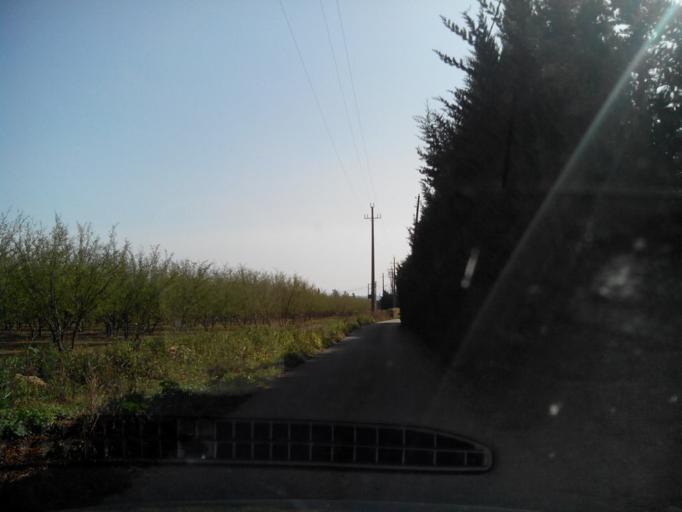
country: ES
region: Catalonia
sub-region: Provincia de Tarragona
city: La Selva
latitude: 41.2114
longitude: 1.1706
